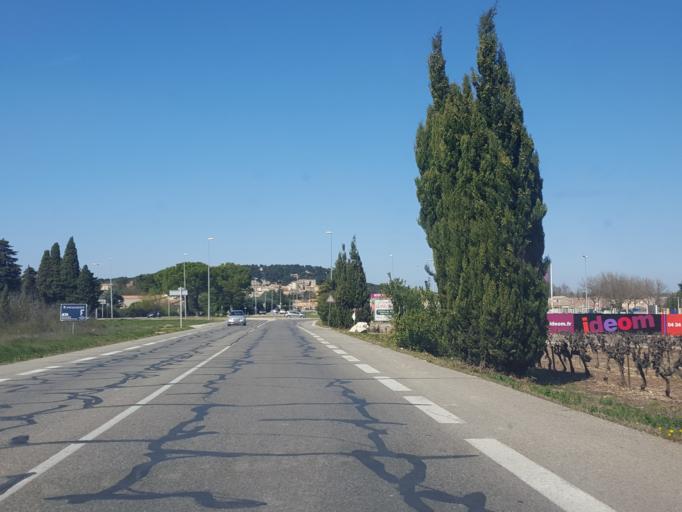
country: FR
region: Provence-Alpes-Cote d'Azur
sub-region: Departement du Vaucluse
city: Vedene
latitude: 43.9723
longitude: 4.9146
